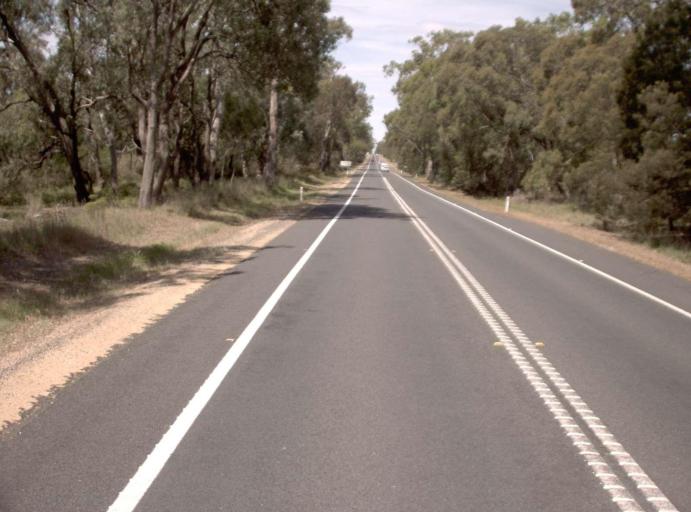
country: AU
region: Victoria
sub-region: Wellington
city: Sale
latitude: -37.9366
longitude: 147.1612
